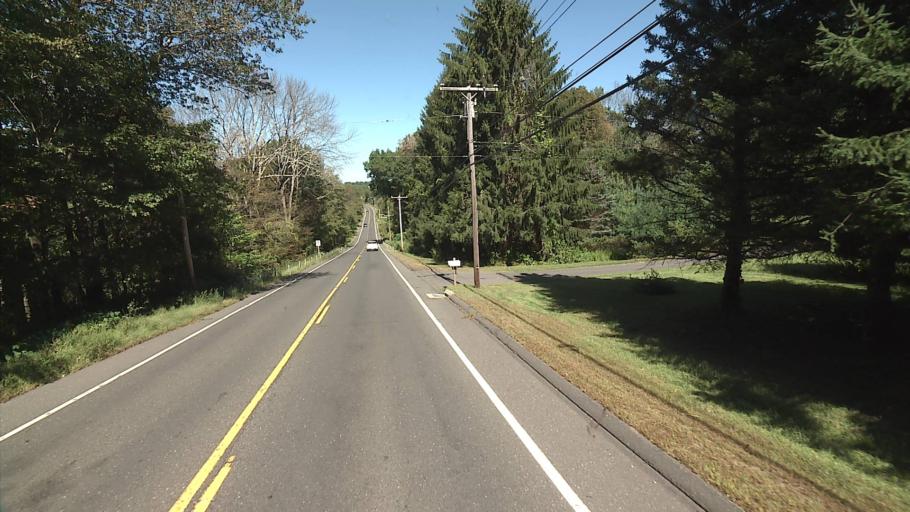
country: US
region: Connecticut
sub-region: New Haven County
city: Prospect
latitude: 41.4787
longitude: -72.9698
